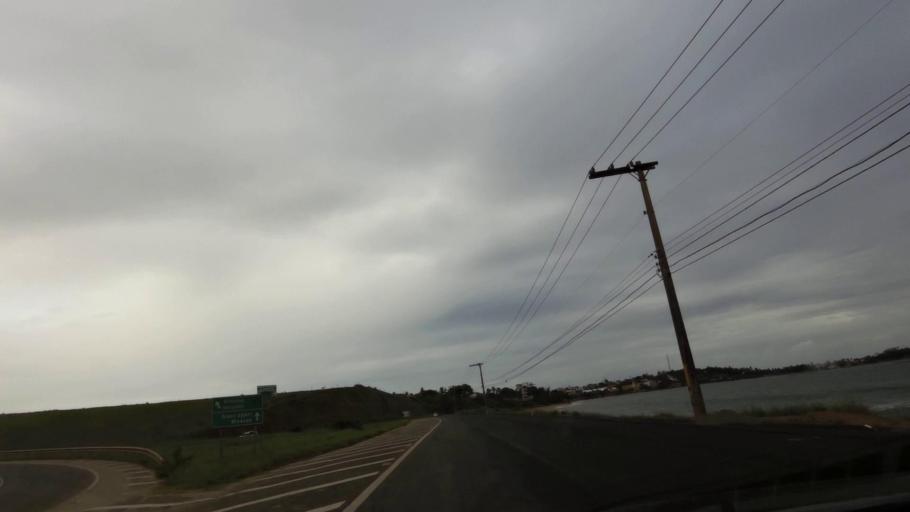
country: BR
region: Espirito Santo
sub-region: Guarapari
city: Guarapari
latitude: -20.7410
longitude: -40.5505
